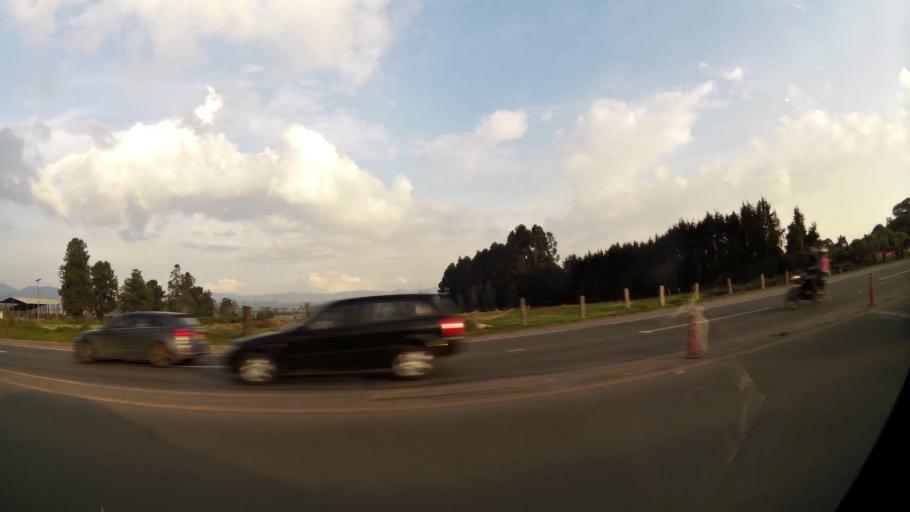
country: CO
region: Cundinamarca
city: Cota
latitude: 4.7893
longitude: -74.1191
